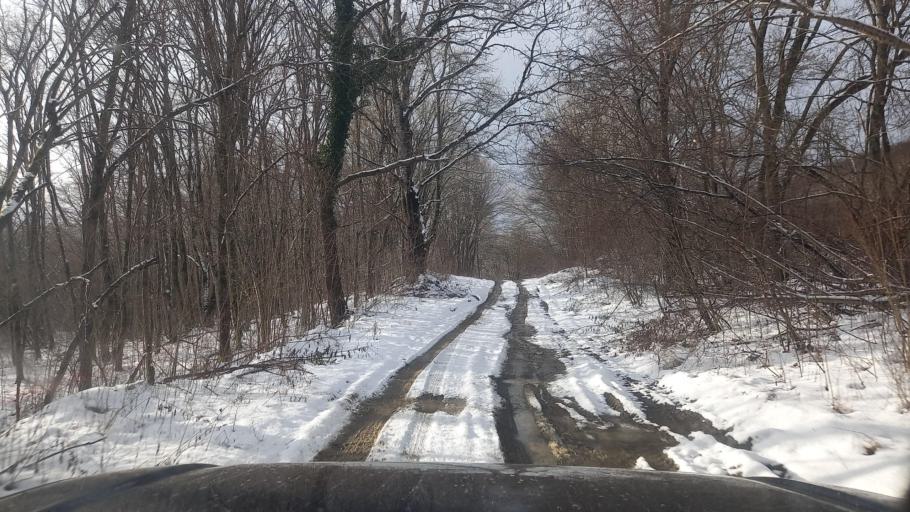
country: RU
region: Krasnodarskiy
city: Smolenskaya
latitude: 44.6846
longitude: 38.8784
